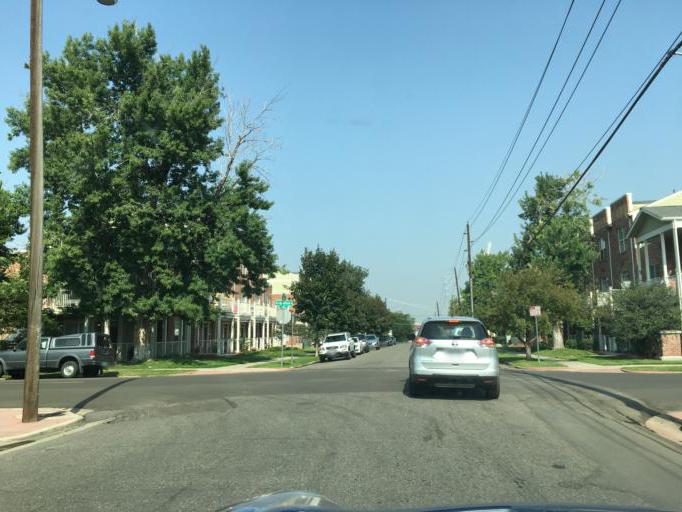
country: US
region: Colorado
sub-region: Denver County
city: Denver
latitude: 39.7627
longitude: -104.9762
